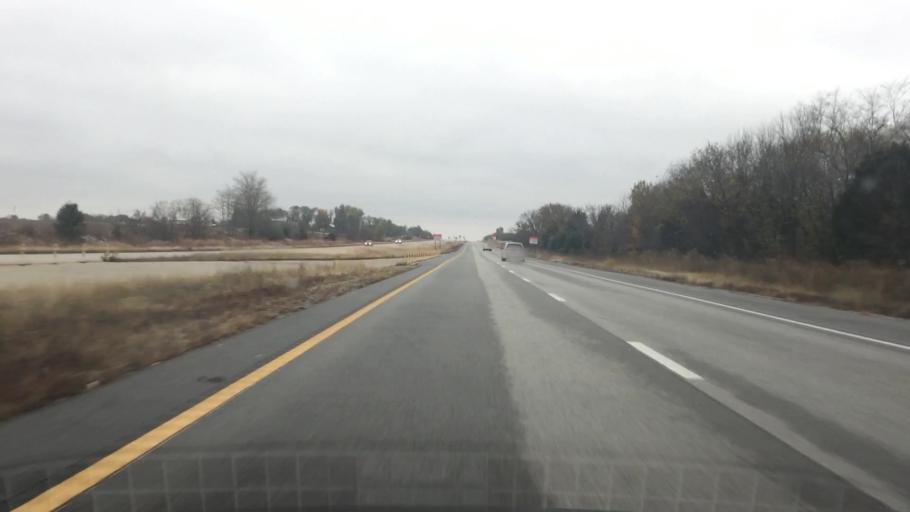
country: US
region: Missouri
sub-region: Henry County
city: Clinton
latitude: 38.3057
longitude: -93.7587
